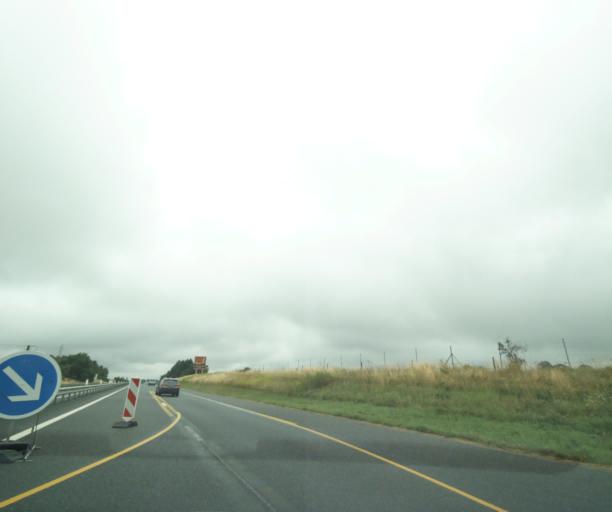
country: FR
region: Midi-Pyrenees
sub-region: Departement de l'Aveyron
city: Luc-la-Primaube
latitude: 44.2957
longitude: 2.5219
